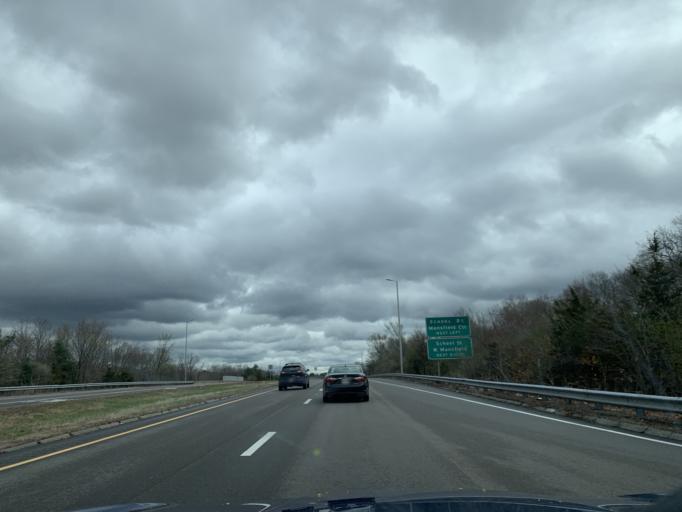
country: US
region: Massachusetts
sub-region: Bristol County
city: Mansfield Center
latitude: 42.0213
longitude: -71.2298
